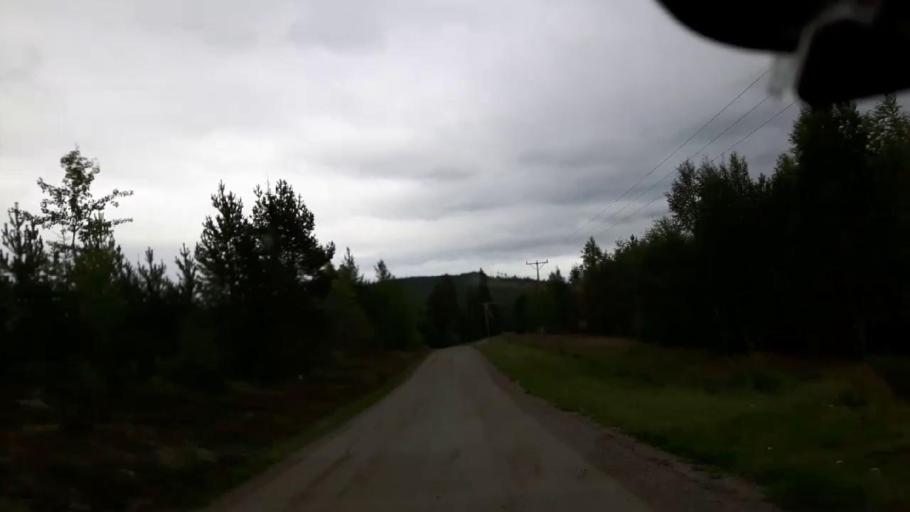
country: SE
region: Vaesternorrland
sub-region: Ange Kommun
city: Fransta
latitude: 62.7786
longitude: 16.2173
